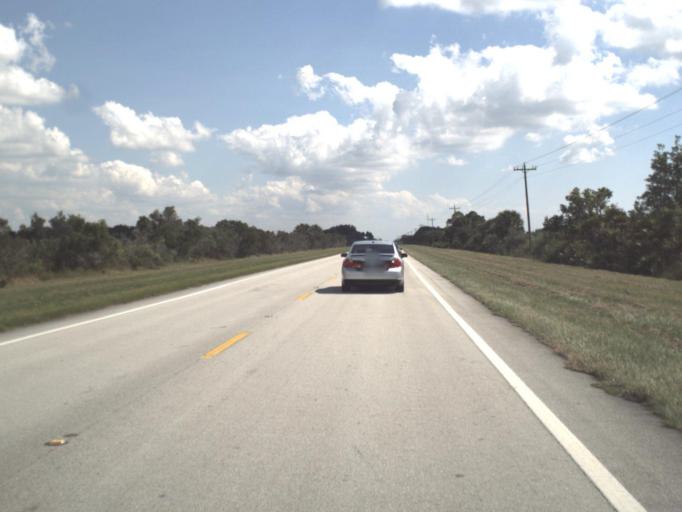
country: US
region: Florida
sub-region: Okeechobee County
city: Okeechobee
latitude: 27.3667
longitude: -80.9726
